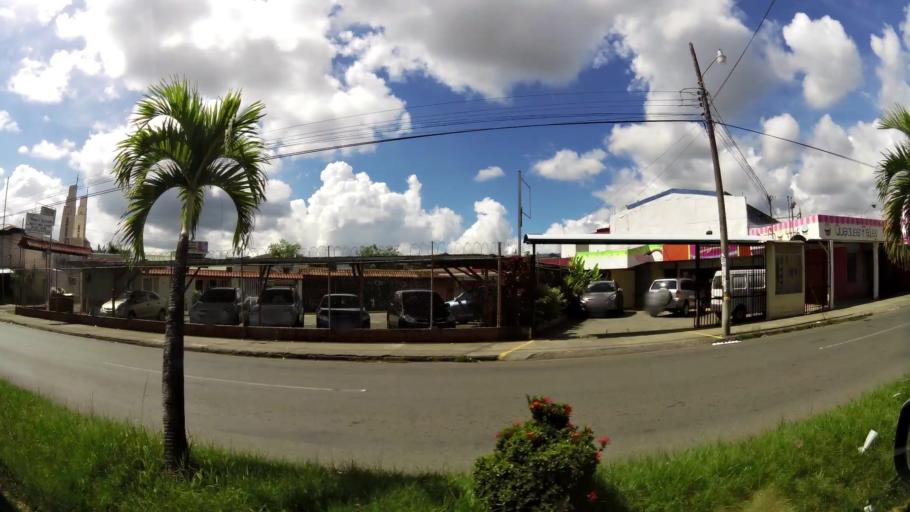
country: CR
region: San Jose
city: San Isidro
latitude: 9.3752
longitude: -83.7024
